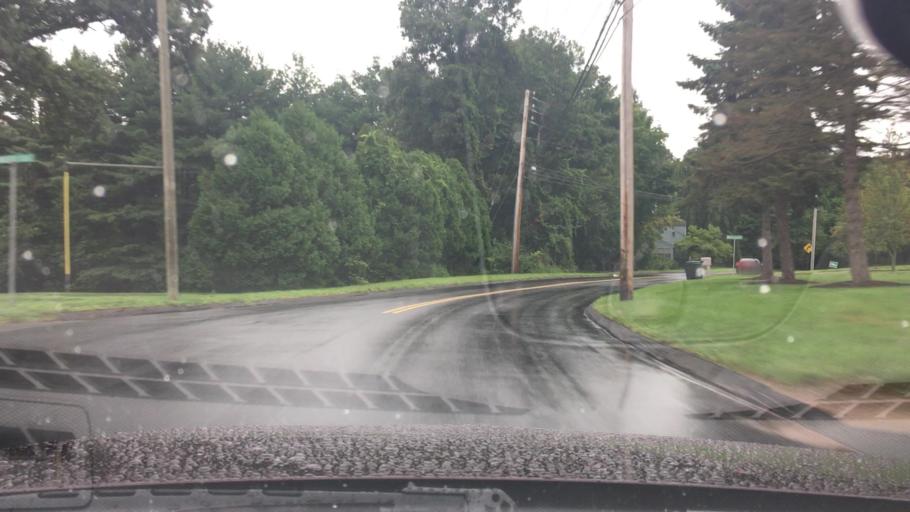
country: US
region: Connecticut
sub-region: New Haven County
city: Cheshire Village
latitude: 41.5270
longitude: -72.9152
